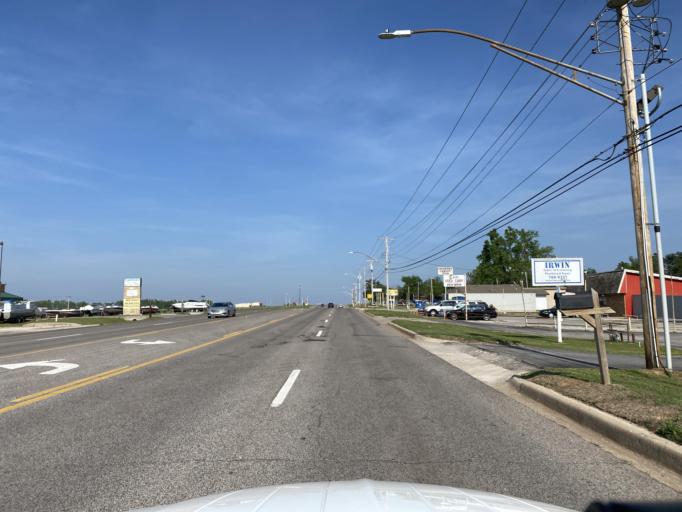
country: US
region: Oklahoma
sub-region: Oklahoma County
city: Nicoma Park
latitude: 35.4930
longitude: -97.3487
